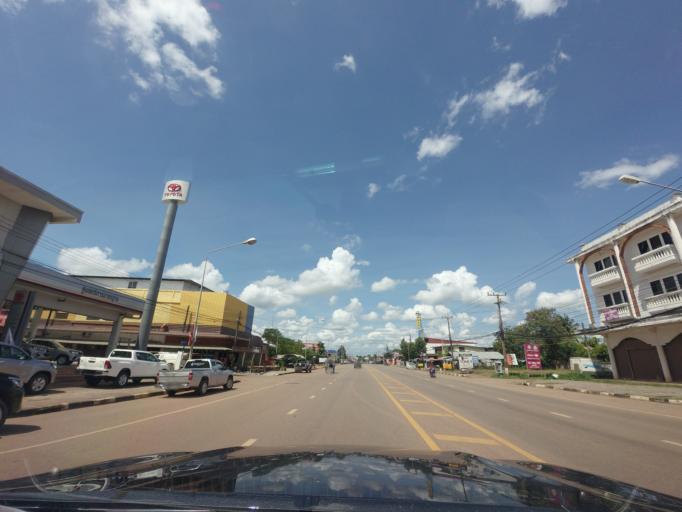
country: TH
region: Changwat Udon Thani
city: Ban Dung
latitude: 17.6869
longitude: 103.2564
